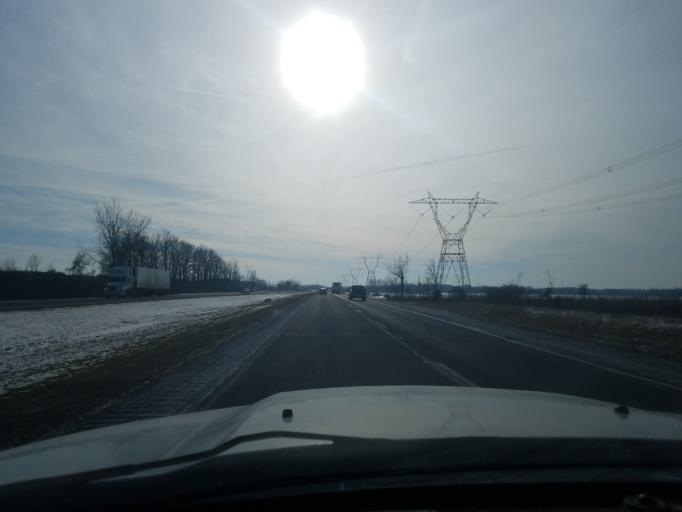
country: US
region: Indiana
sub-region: Huntington County
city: Roanoke
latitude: 40.9385
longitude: -85.3087
